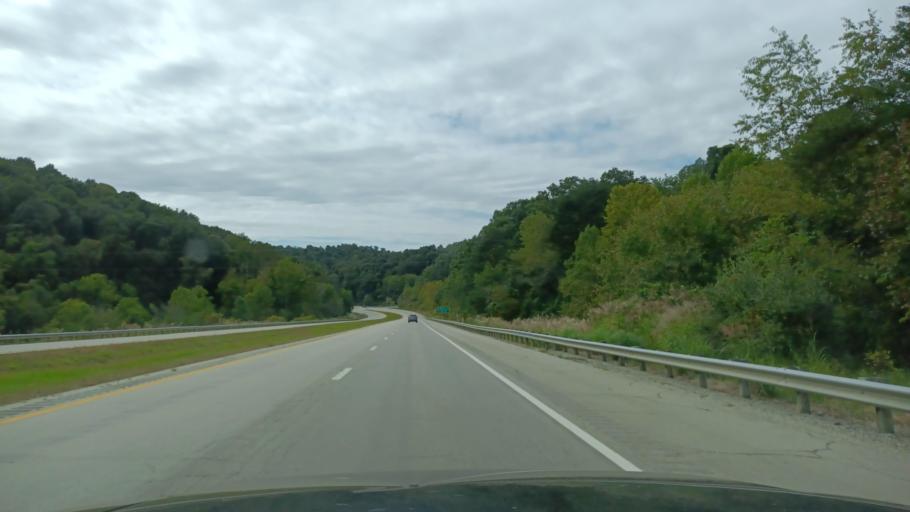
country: US
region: Ohio
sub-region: Washington County
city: Newport
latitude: 39.2593
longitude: -81.2844
